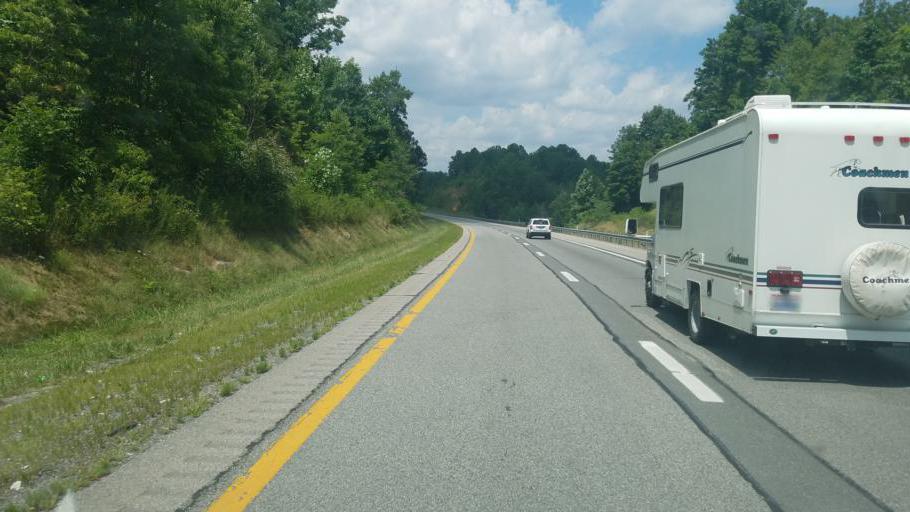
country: US
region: West Virginia
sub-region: Raleigh County
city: Bradley
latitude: 37.8902
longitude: -81.2657
